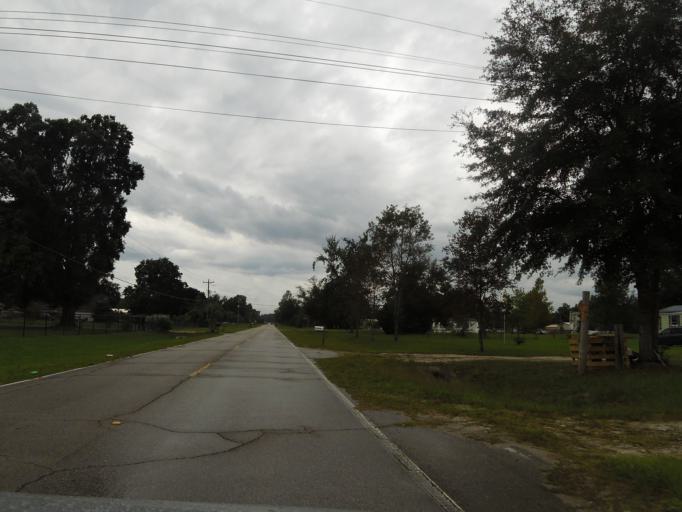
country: US
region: Florida
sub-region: Clay County
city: Middleburg
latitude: 30.1179
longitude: -81.9618
